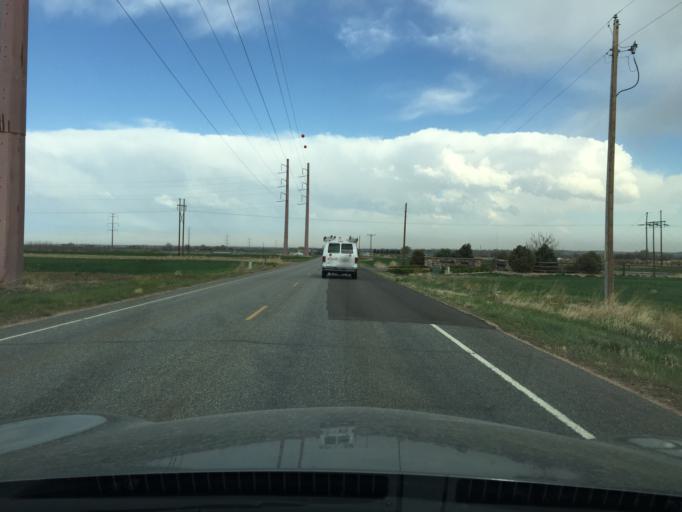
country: US
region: Colorado
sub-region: Boulder County
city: Gunbarrel
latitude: 40.0729
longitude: -105.1166
